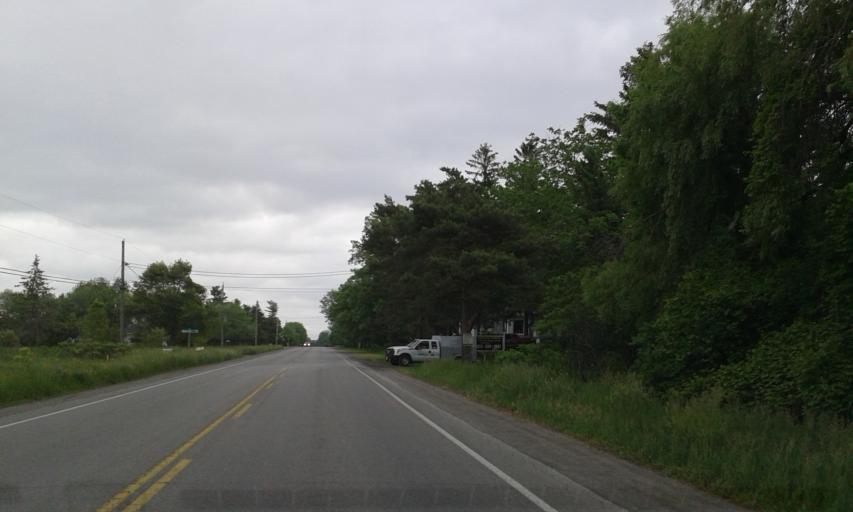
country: CA
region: Ontario
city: Prince Edward
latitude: 43.9599
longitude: -77.3125
